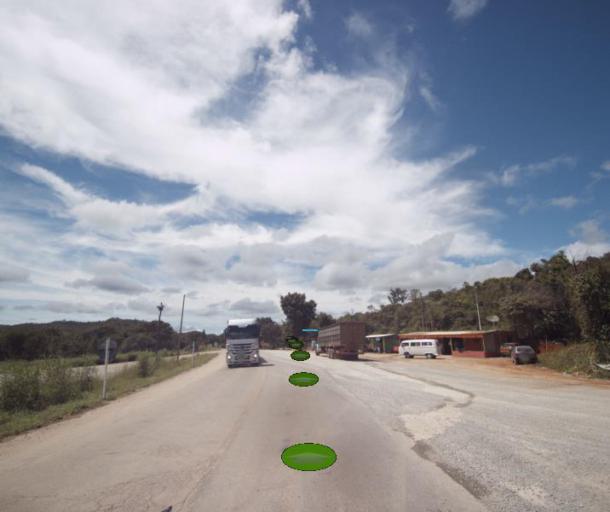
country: BR
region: Goias
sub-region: Padre Bernardo
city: Padre Bernardo
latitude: -15.5010
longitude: -48.2194
